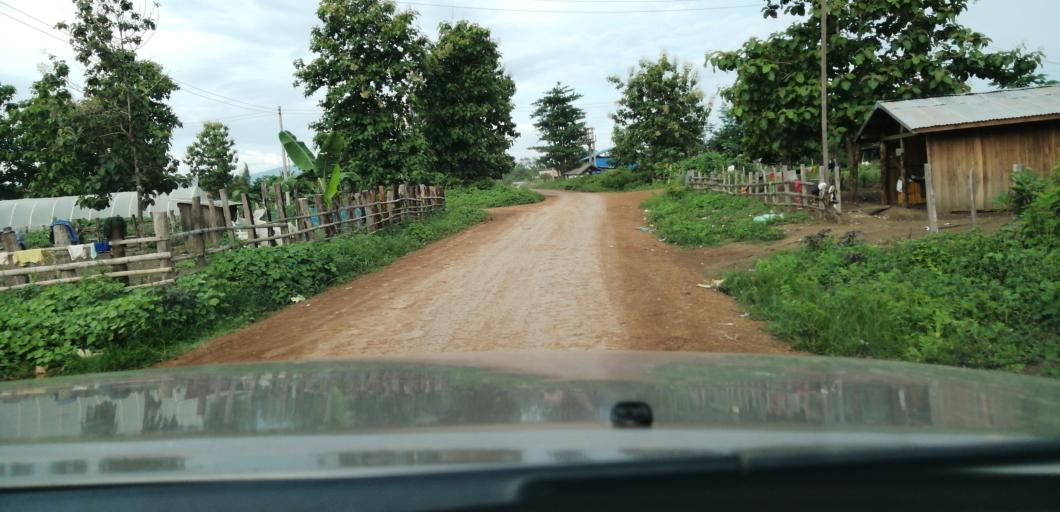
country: LA
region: Attapu
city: Attapu
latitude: 14.7067
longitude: 106.4460
